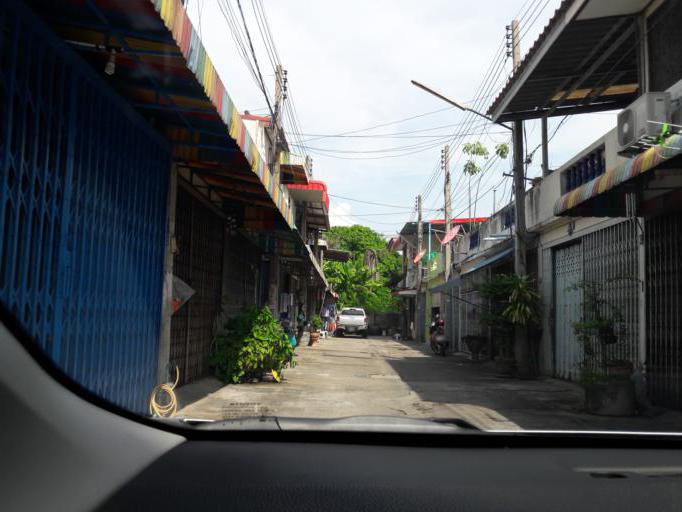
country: TH
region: Ang Thong
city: Ang Thong
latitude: 14.5898
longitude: 100.4472
